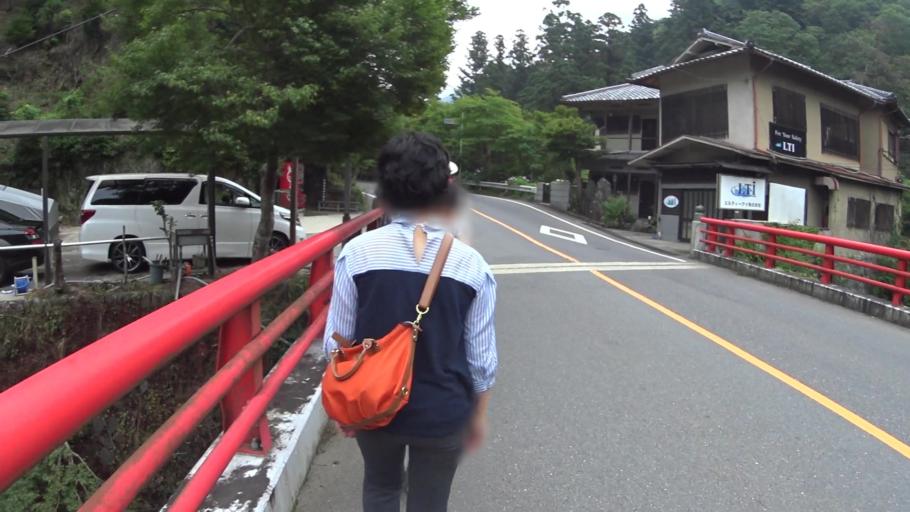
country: JP
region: Kyoto
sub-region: Kyoto-shi
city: Kamigyo-ku
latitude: 35.0583
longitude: 135.6776
